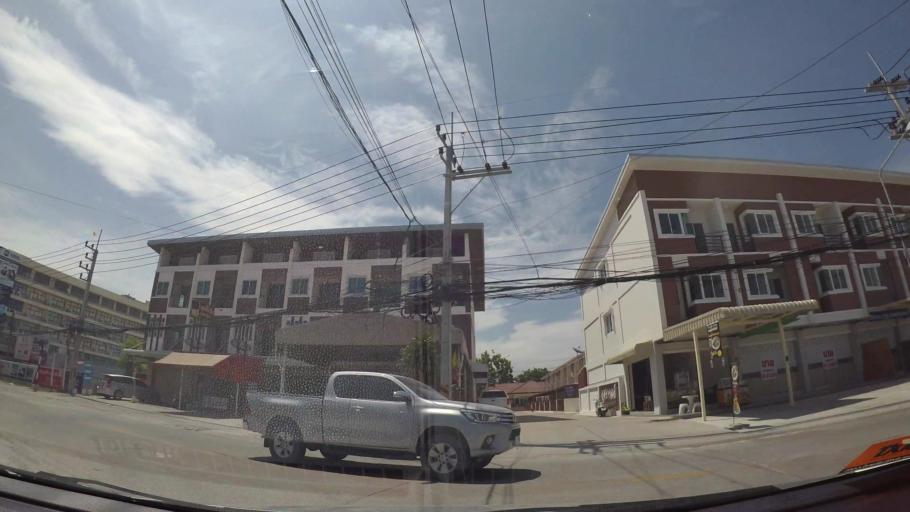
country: TH
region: Chon Buri
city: Chon Buri
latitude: 13.3218
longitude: 100.9560
